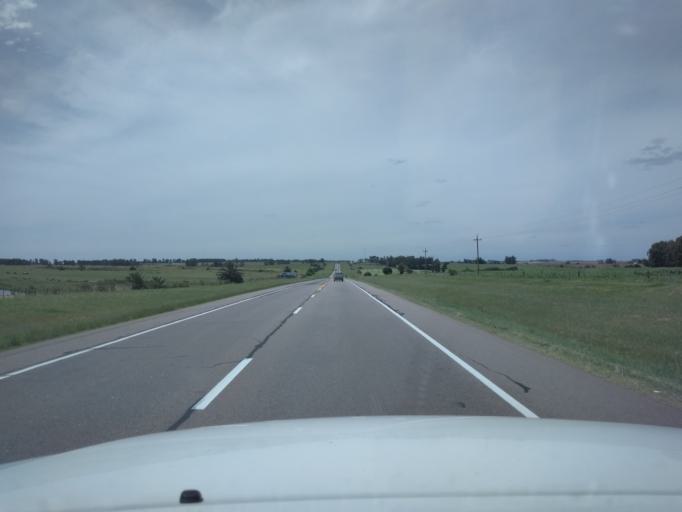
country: UY
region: Florida
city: Florida
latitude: -34.2257
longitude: -56.2108
